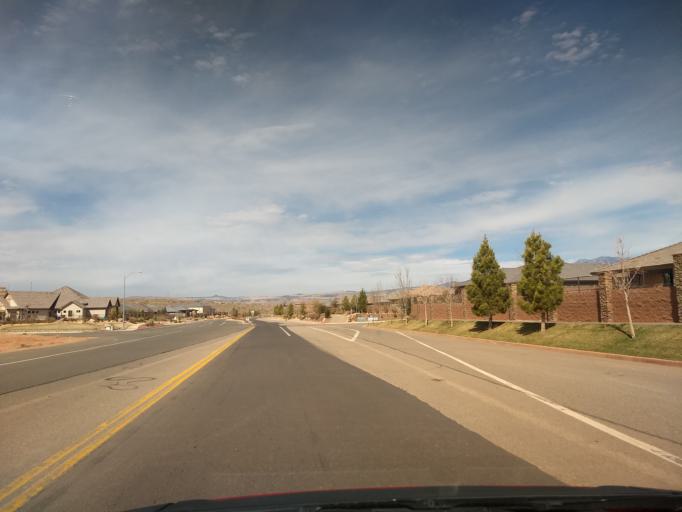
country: US
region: Utah
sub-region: Washington County
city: Washington
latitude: 37.0670
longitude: -113.4917
